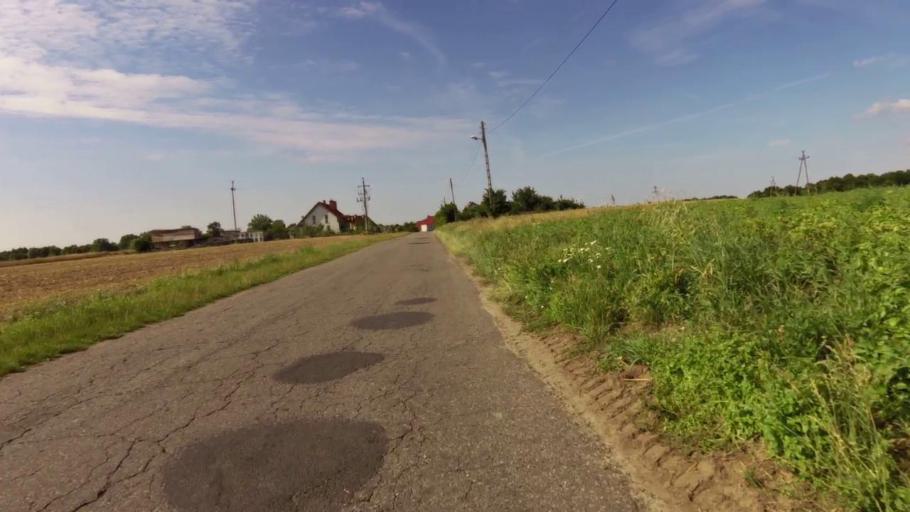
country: PL
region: West Pomeranian Voivodeship
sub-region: Powiat stargardzki
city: Marianowo
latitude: 53.3467
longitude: 15.1950
